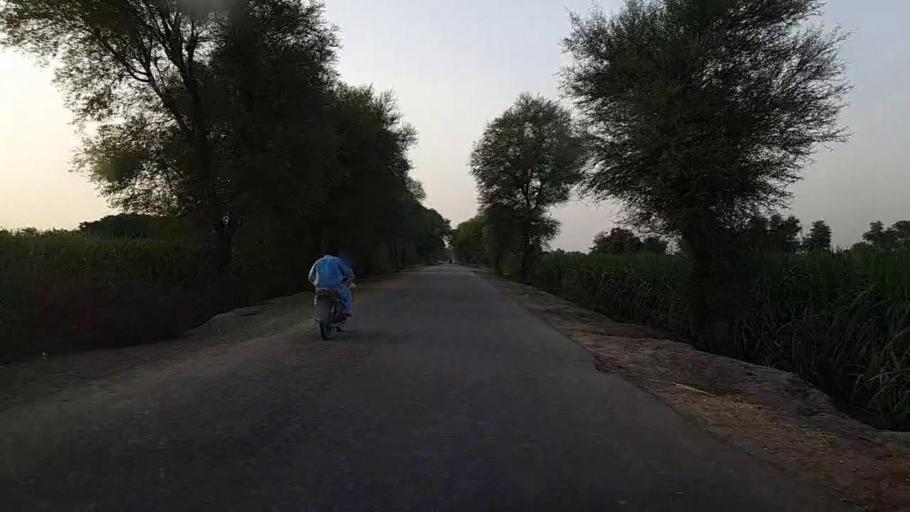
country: PK
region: Sindh
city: Ubauro
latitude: 28.2376
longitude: 69.8133
